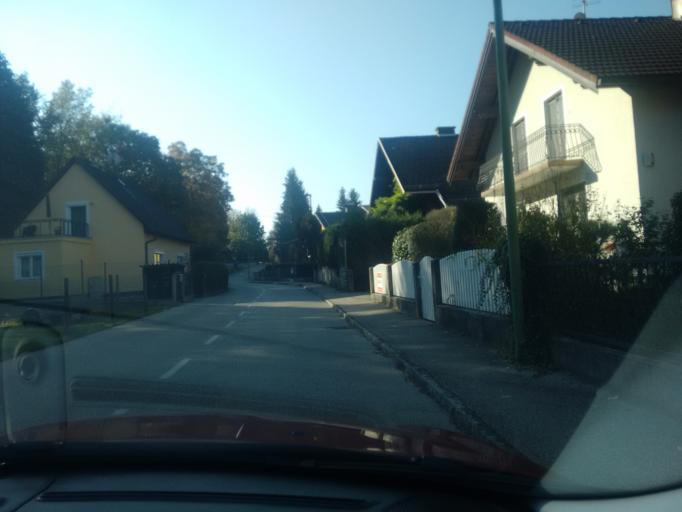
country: AT
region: Upper Austria
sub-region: Wels-Land
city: Steinhaus
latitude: 48.1400
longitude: 14.0088
